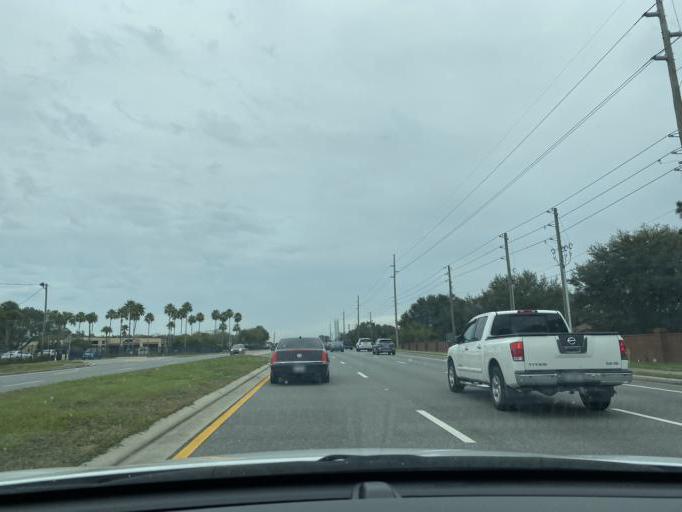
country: US
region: Florida
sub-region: Orange County
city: Oakland
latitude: 28.5462
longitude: -81.6490
